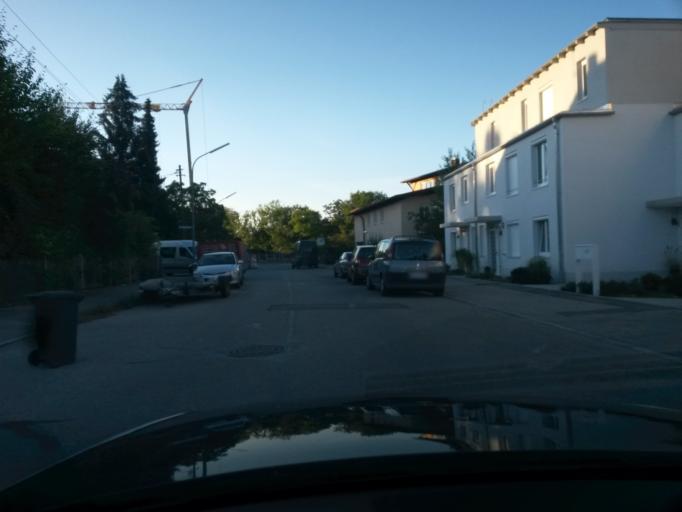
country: DE
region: Bavaria
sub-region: Upper Bavaria
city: Karlsfeld
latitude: 48.1955
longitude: 11.4613
